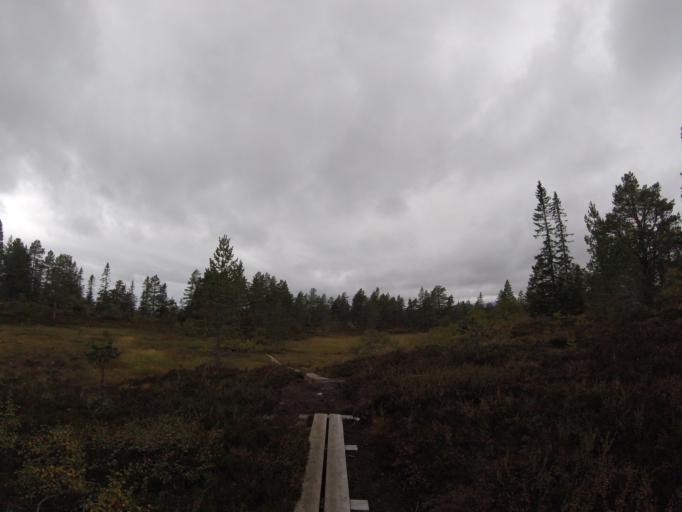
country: NO
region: Buskerud
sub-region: Flesberg
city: Lampeland
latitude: 59.7584
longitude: 9.3953
